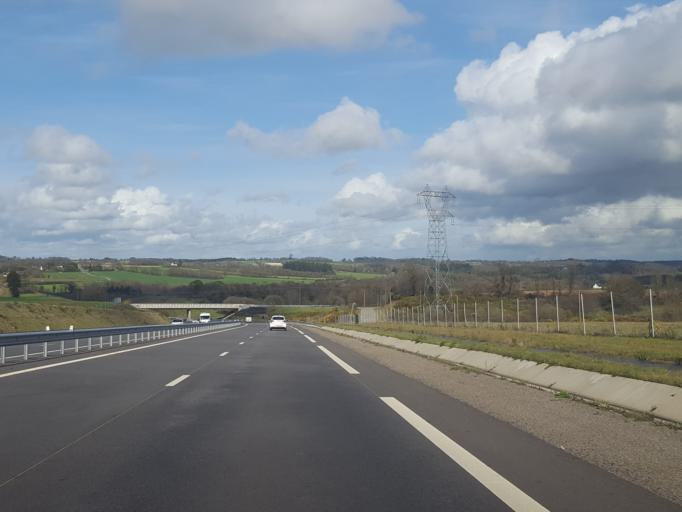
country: FR
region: Brittany
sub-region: Departement d'Ille-et-Vilaine
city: Guignen
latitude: 47.9349
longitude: -1.8356
